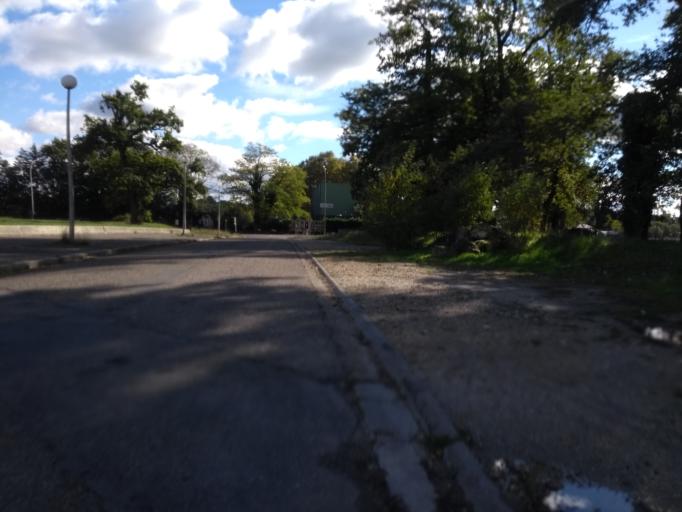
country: FR
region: Aquitaine
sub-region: Departement de la Gironde
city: Gradignan
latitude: 44.7939
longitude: -0.6179
